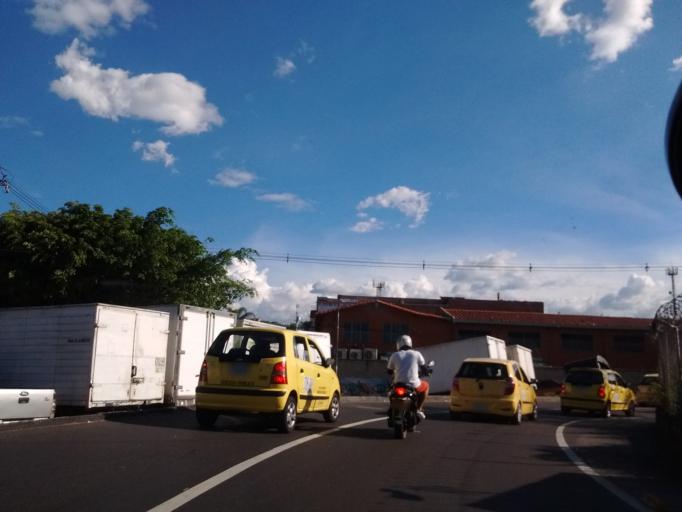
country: CO
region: Antioquia
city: Medellin
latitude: 6.2748
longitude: -75.5719
